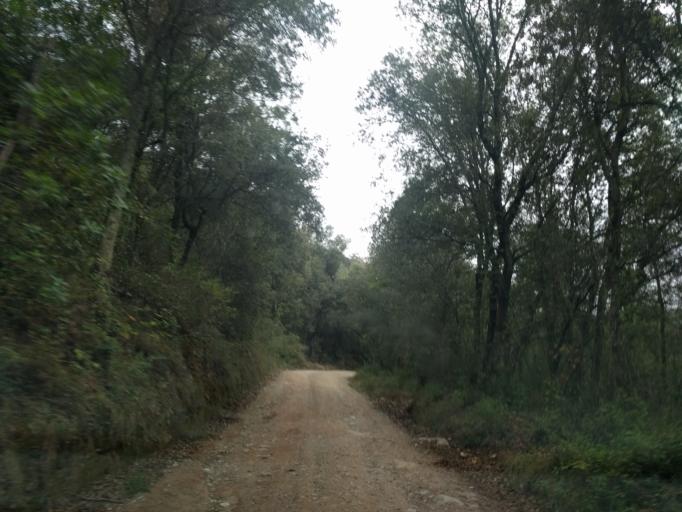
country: ES
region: Catalonia
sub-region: Provincia de Girona
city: la Cellera de Ter
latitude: 42.0108
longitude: 2.6325
